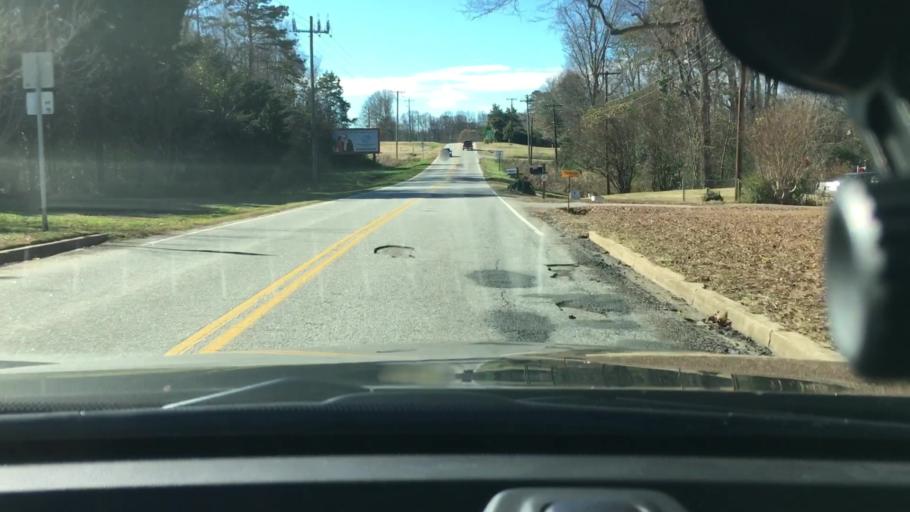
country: US
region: South Carolina
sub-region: Cherokee County
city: East Gaffney
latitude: 35.0911
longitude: -81.6355
